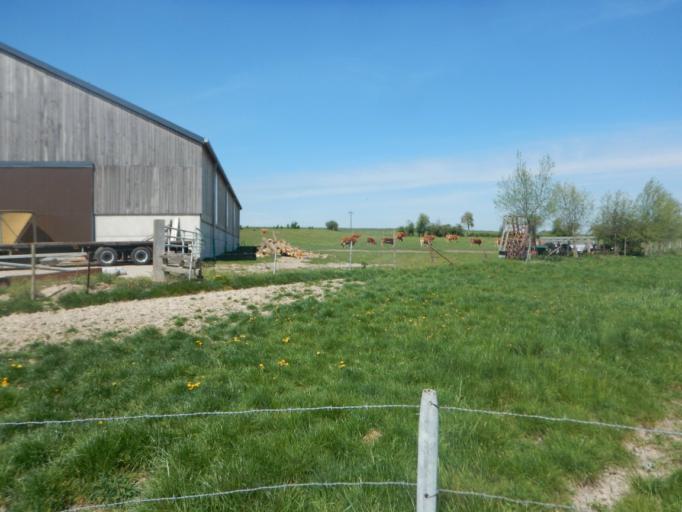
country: LU
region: Diekirch
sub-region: Canton de Redange
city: Redange-sur-Attert
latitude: 49.7550
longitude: 5.9251
